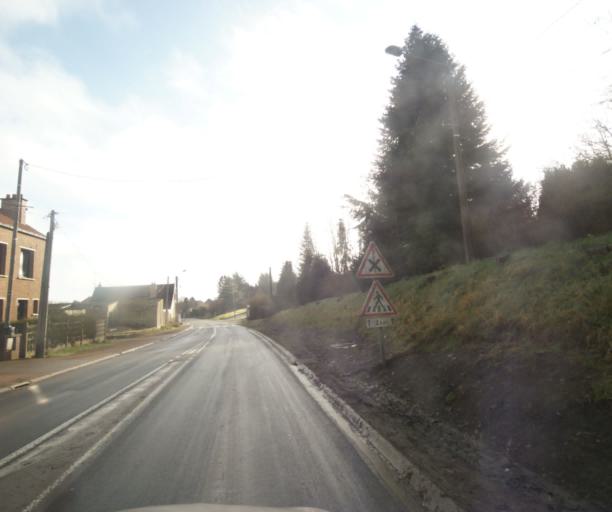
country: FR
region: Nord-Pas-de-Calais
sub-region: Departement du Nord
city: Saulzoir
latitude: 50.2693
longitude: 3.4635
